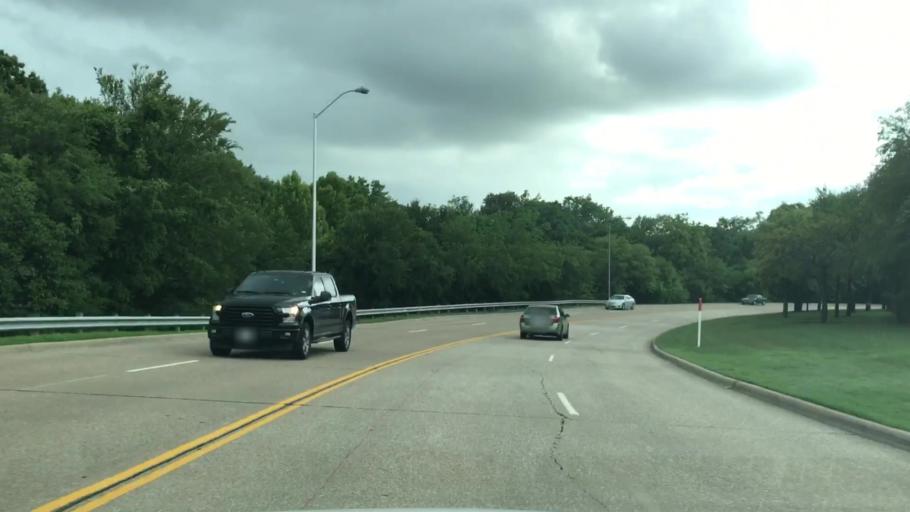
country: US
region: Texas
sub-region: Dallas County
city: Richardson
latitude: 32.9153
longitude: -96.7543
